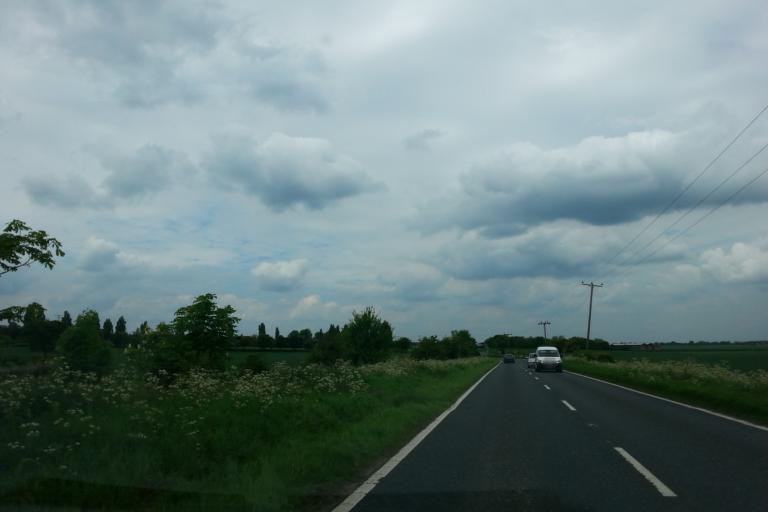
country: GB
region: England
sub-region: Cambridgeshire
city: Ramsey
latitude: 52.4253
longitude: -0.1050
